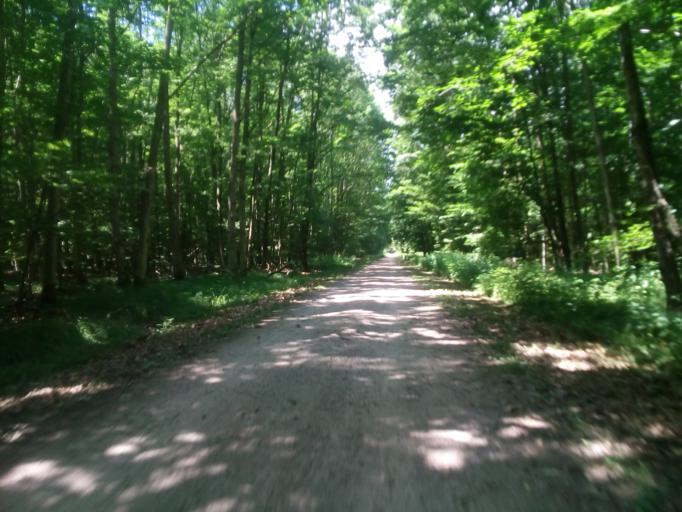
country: DE
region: Baden-Wuerttemberg
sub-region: Freiburg Region
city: Rheinau
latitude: 48.6390
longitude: 7.9603
